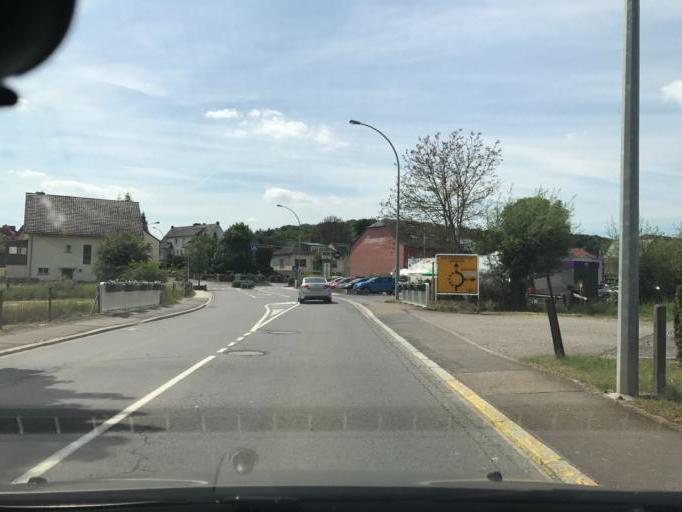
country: LU
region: Luxembourg
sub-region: Canton de Luxembourg
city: Schuttrange
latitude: 49.6342
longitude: 6.2670
